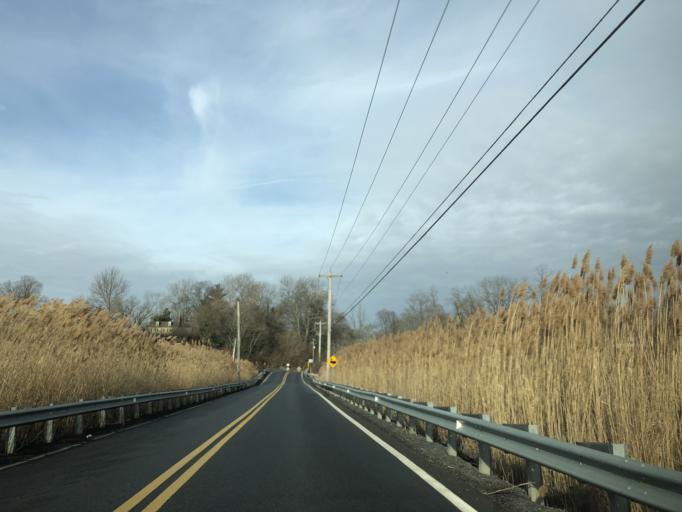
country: US
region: Delaware
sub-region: New Castle County
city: Middletown
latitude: 39.4519
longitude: -75.6534
